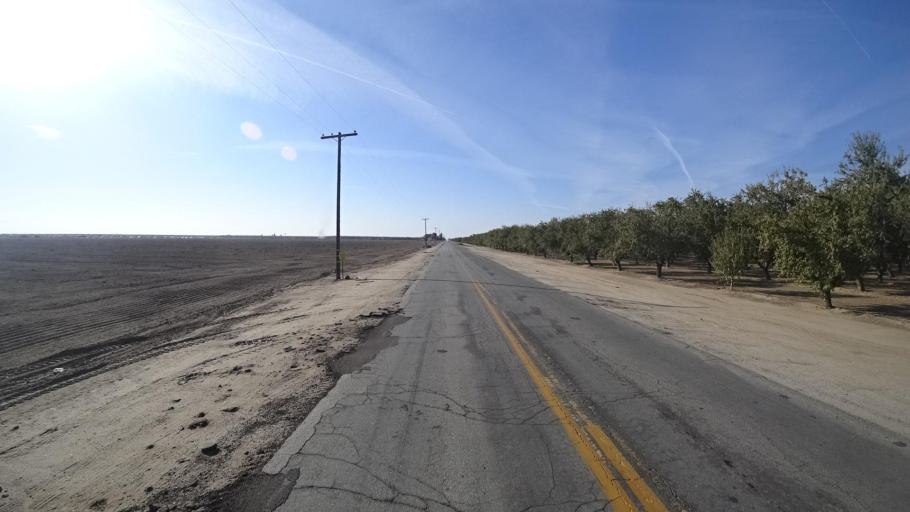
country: US
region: California
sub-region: Kern County
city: McFarland
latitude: 35.7033
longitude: -119.2416
